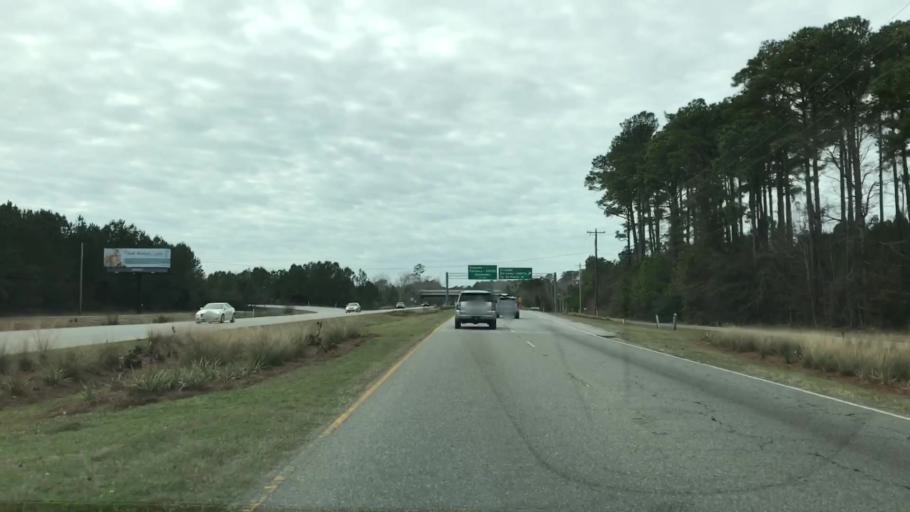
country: US
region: South Carolina
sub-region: Horry County
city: Myrtle Beach
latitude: 33.7411
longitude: -78.8454
